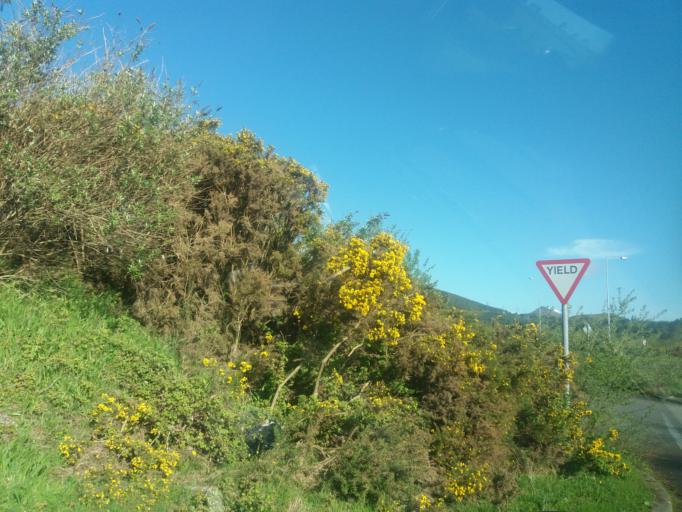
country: IE
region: Leinster
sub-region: Wicklow
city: Kilpedder
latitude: 53.1166
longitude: -6.0988
